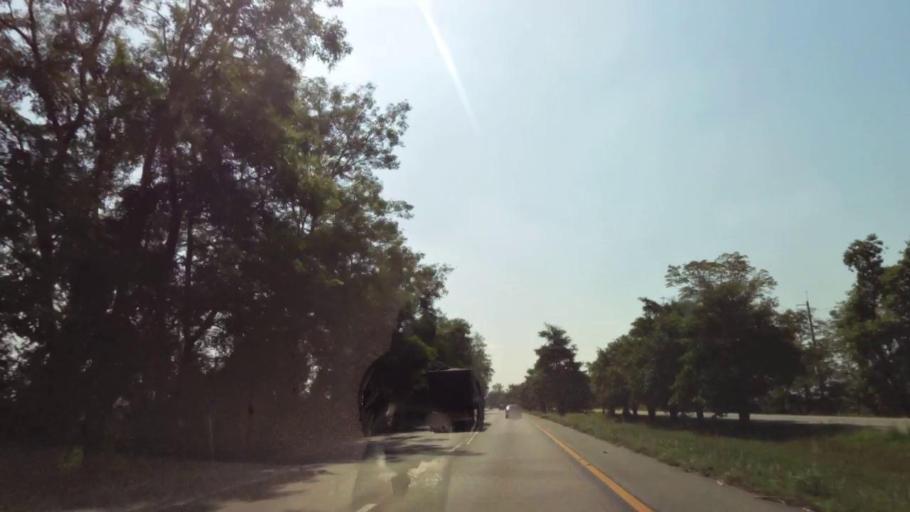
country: TH
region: Phitsanulok
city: Bang Rakam
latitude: 16.6469
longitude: 100.1505
